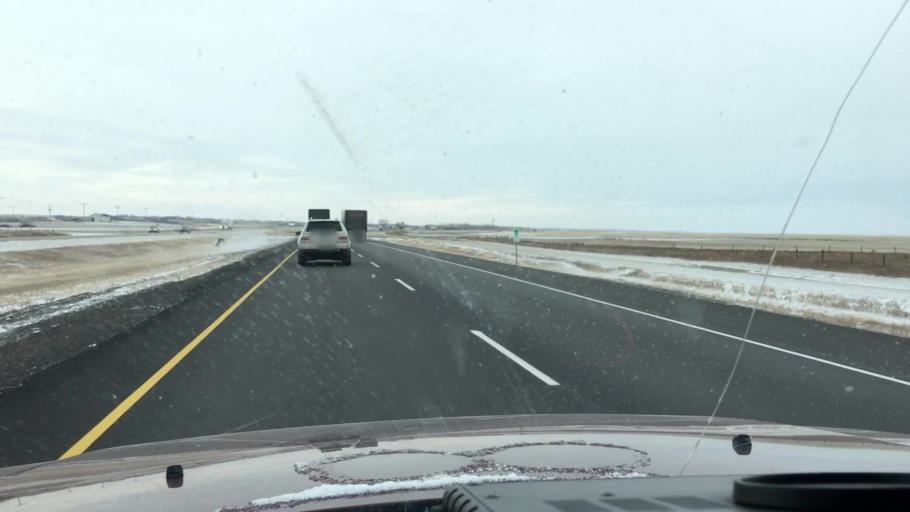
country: CA
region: Saskatchewan
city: Saskatoon
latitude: 51.7841
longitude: -106.4794
